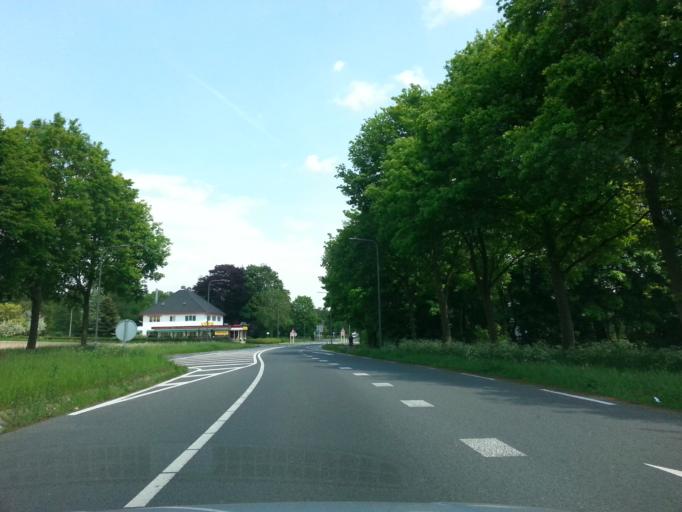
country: NL
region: Gelderland
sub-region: Gemeente Rheden
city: Rheden
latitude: 52.0044
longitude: 6.0029
